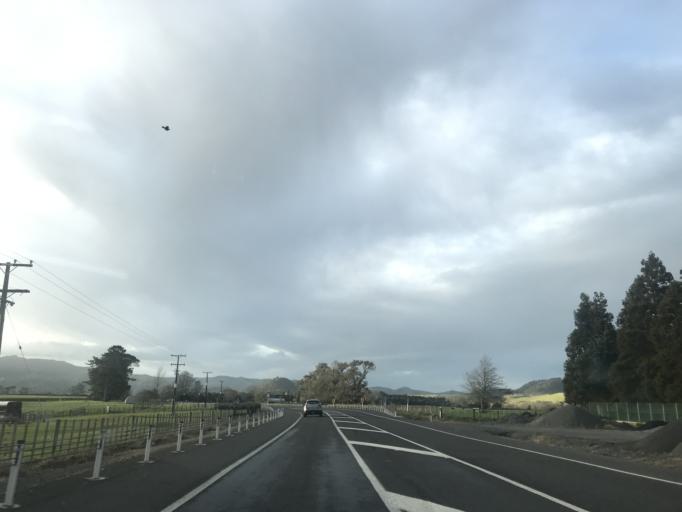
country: NZ
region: Waikato
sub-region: Hauraki District
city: Waihi
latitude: -37.4257
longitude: 175.8701
